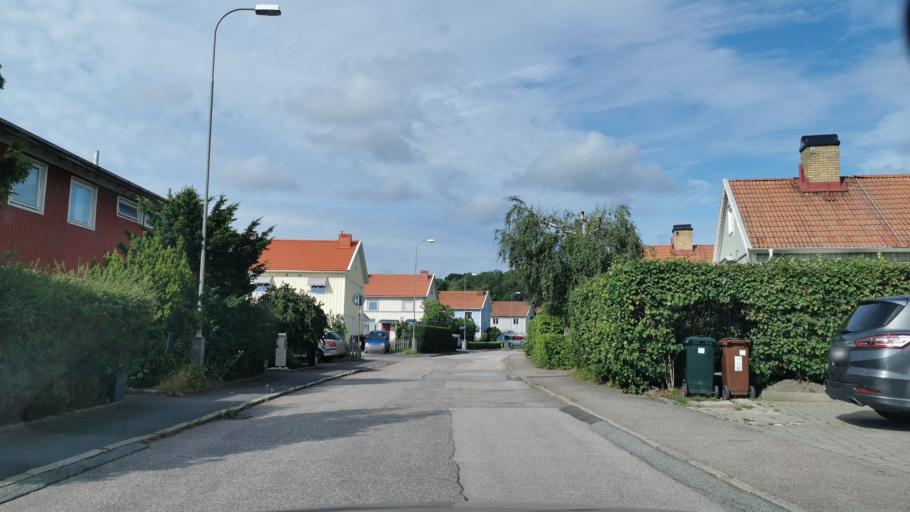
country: SE
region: Vaestra Goetaland
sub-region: Goteborg
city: Majorna
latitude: 57.6510
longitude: 11.9289
